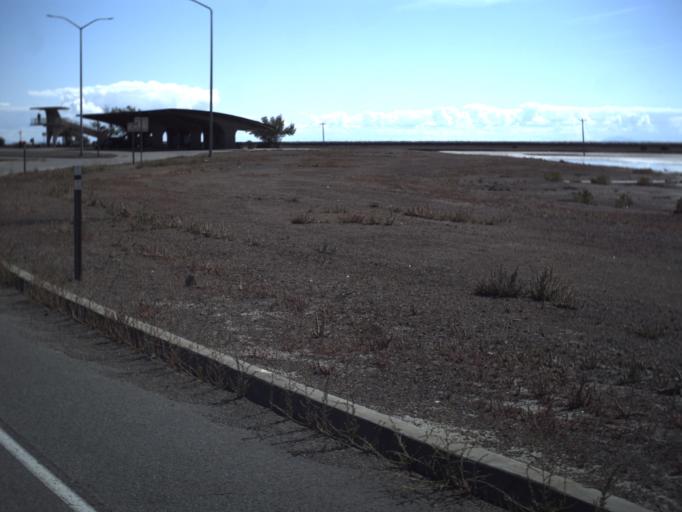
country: US
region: Utah
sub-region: Tooele County
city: Wendover
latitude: 40.7385
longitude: -113.8593
